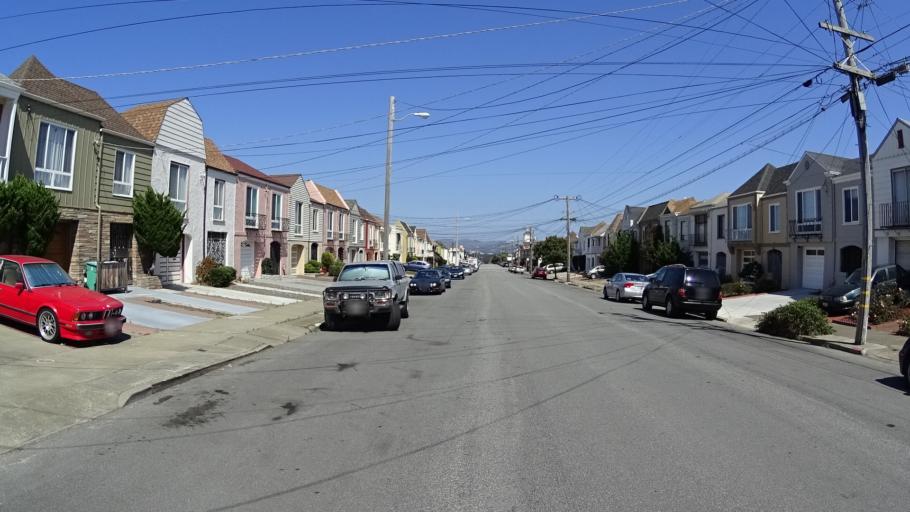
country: US
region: California
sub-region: San Mateo County
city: Daly City
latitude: 37.7524
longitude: -122.4871
